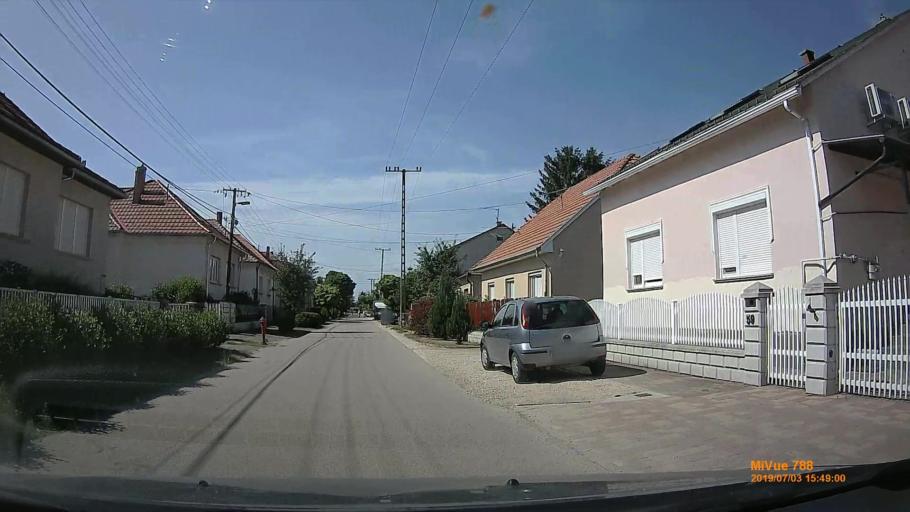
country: HU
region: Gyor-Moson-Sopron
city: Toltestava
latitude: 47.6955
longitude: 17.7352
